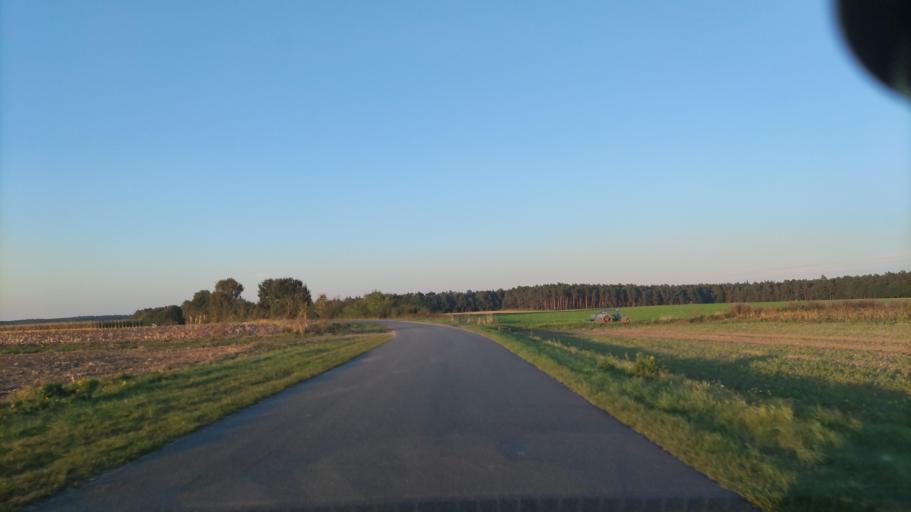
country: DE
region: Lower Saxony
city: Bispingen
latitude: 53.0775
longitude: 10.0176
